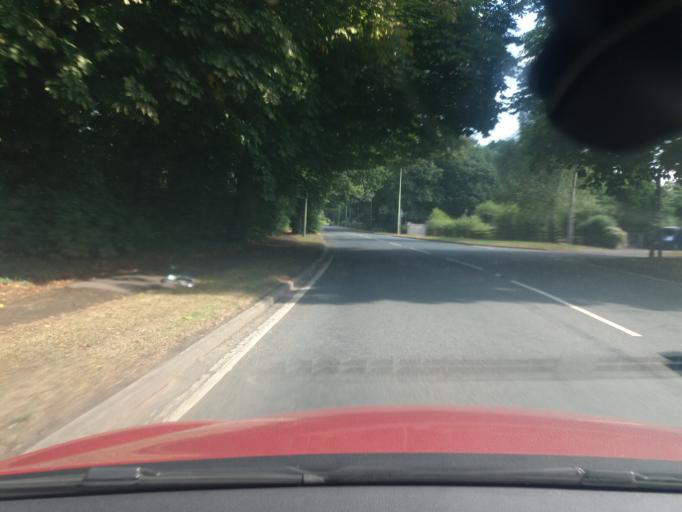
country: GB
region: England
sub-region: Lancashire
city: Adlington
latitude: 53.6284
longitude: -2.6173
